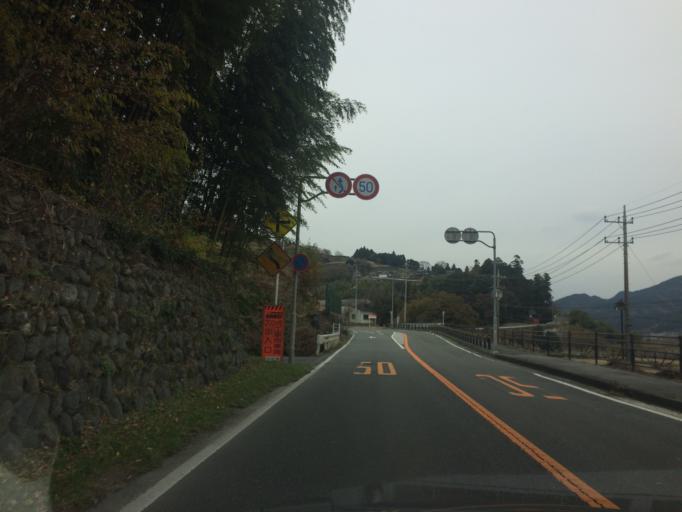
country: JP
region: Shizuoka
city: Fujinomiya
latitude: 35.2611
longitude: 138.4697
